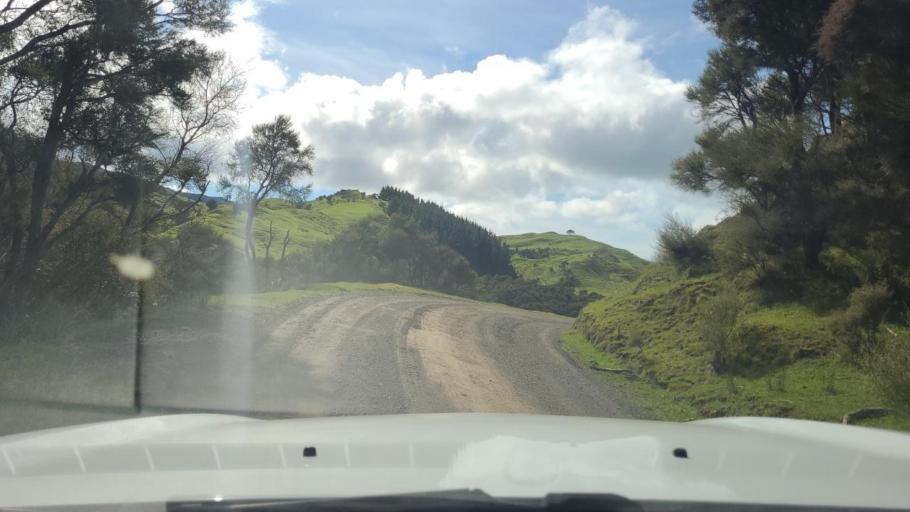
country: NZ
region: Wellington
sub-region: South Wairarapa District
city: Waipawa
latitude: -41.3720
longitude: 175.7130
